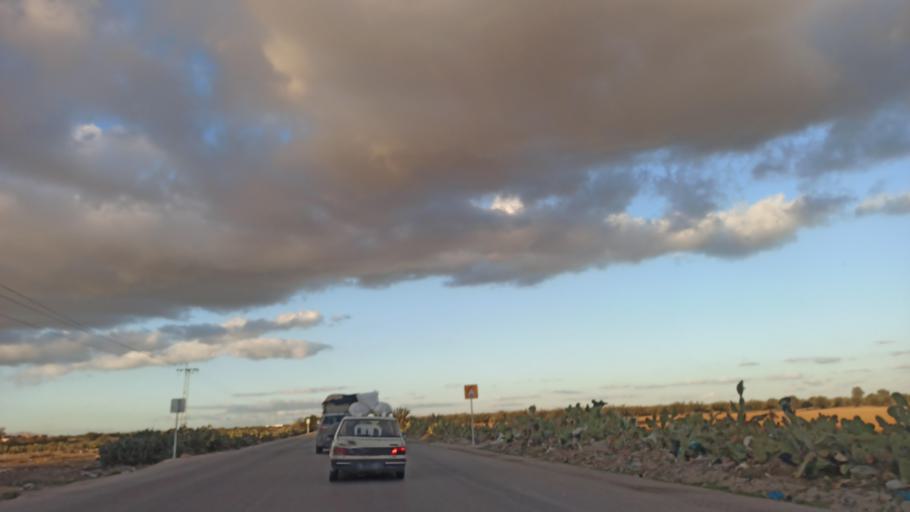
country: TN
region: Susah
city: Sidi Bou Ali
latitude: 36.0124
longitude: 10.3183
